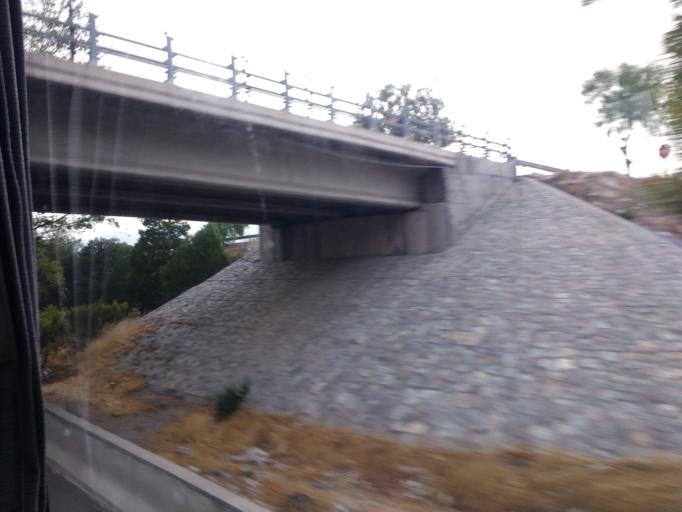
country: CL
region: Santiago Metropolitan
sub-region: Provincia de Santiago
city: Lo Prado
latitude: -33.4431
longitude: -70.8483
